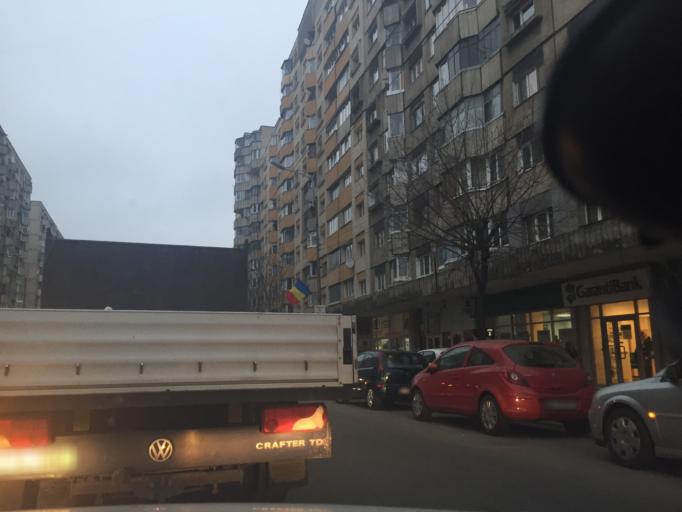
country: RO
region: Cluj
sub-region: Municipiul Cluj-Napoca
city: Cluj-Napoca
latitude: 46.7797
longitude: 23.6140
